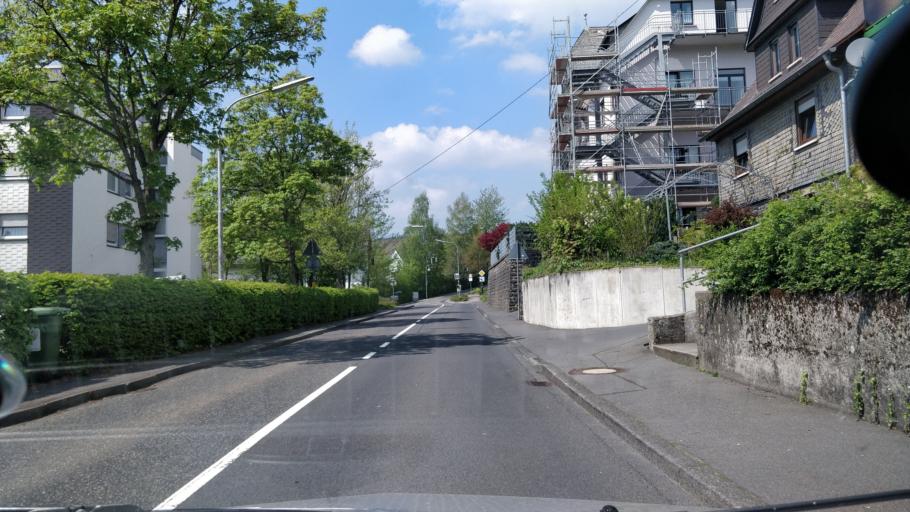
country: DE
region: Rheinland-Pfalz
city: Bad Marienberg
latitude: 50.6484
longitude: 7.9568
